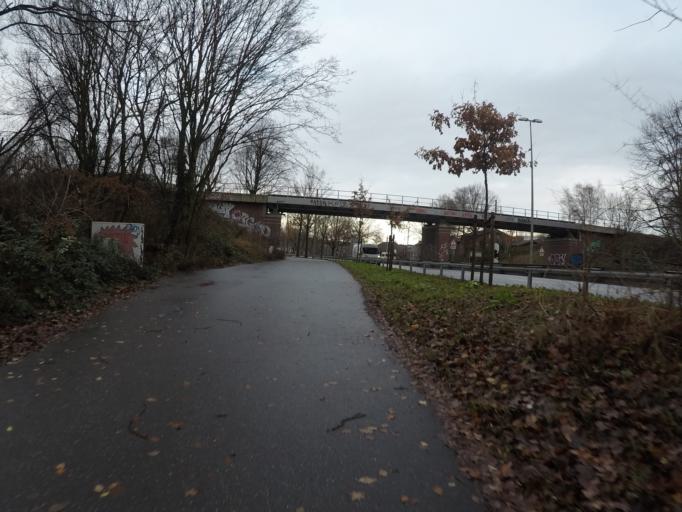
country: DE
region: Hamburg
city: Kleiner Grasbrook
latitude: 53.5195
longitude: 10.0152
